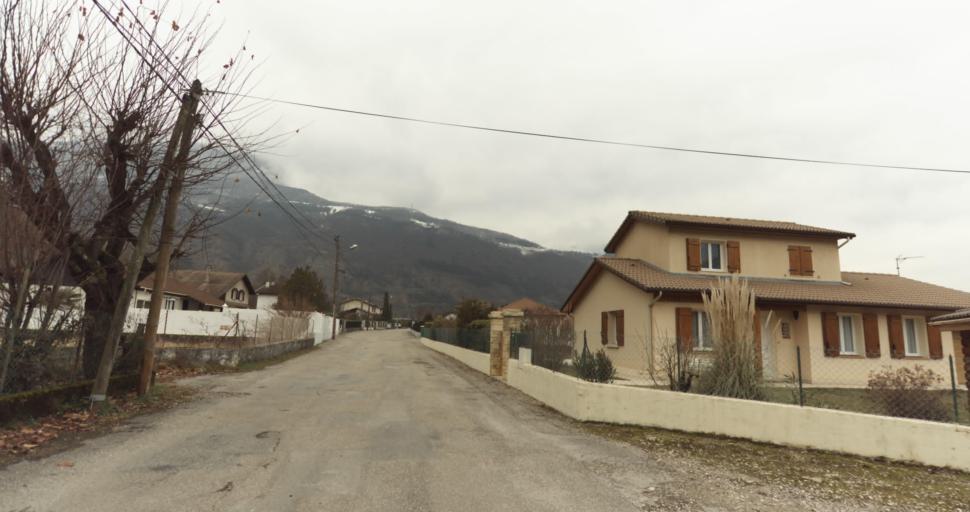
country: FR
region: Rhone-Alpes
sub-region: Departement de l'Isere
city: Vif
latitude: 45.0495
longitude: 5.6751
